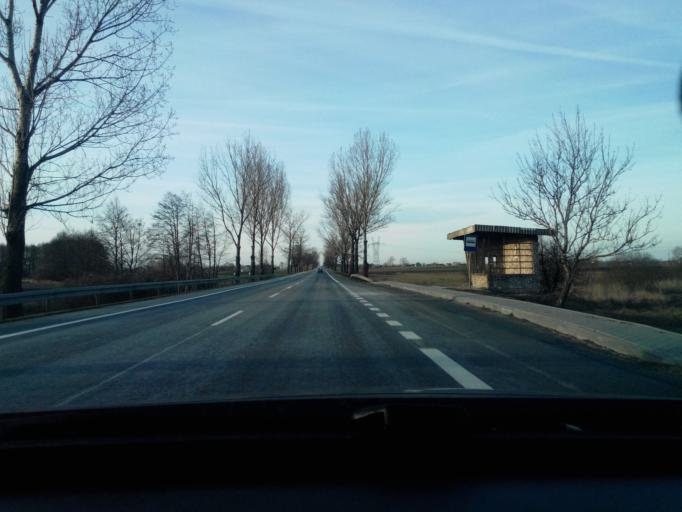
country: PL
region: Kujawsko-Pomorskie
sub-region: Powiat wloclawski
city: Lubien Kujawski
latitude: 52.4272
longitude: 19.1636
